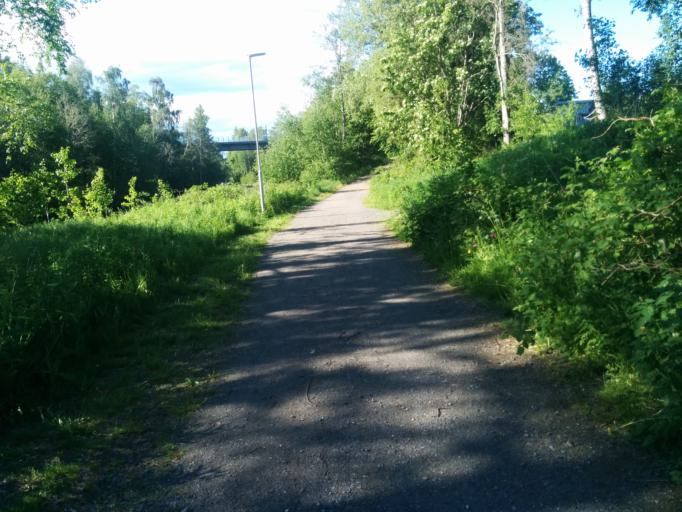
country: SE
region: Vaesterbotten
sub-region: Umea Kommun
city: Hoernefors
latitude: 63.6313
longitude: 19.9120
